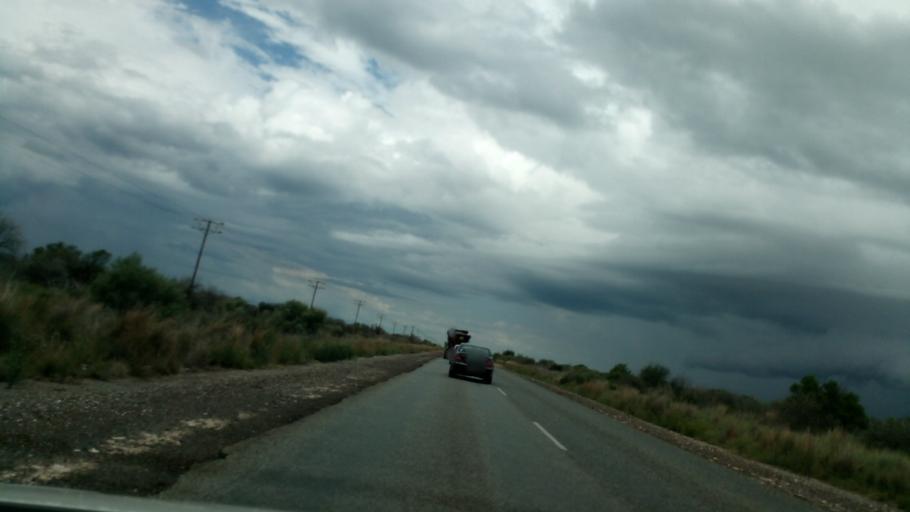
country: ZA
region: Northern Cape
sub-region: Frances Baard District Municipality
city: Barkly West
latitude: -28.2666
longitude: 24.0681
